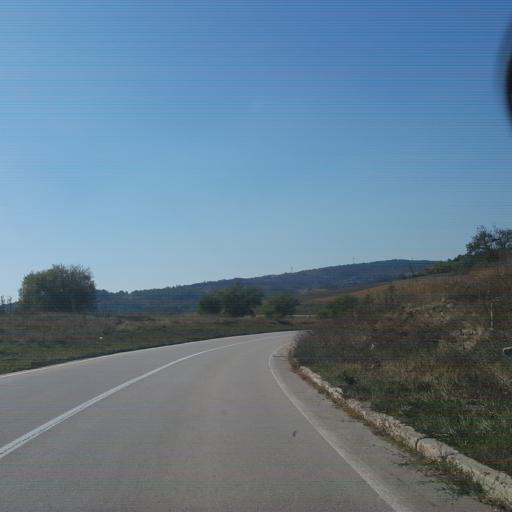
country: RS
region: Central Serbia
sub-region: Nisavski Okrug
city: Svrljig
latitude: 43.4526
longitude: 22.1983
